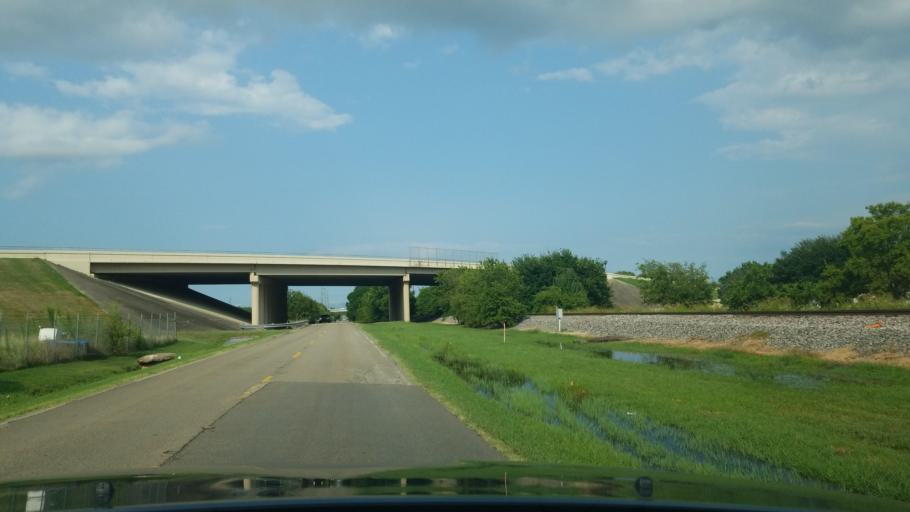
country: US
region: Texas
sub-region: Denton County
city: Denton
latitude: 33.2339
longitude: -97.0978
